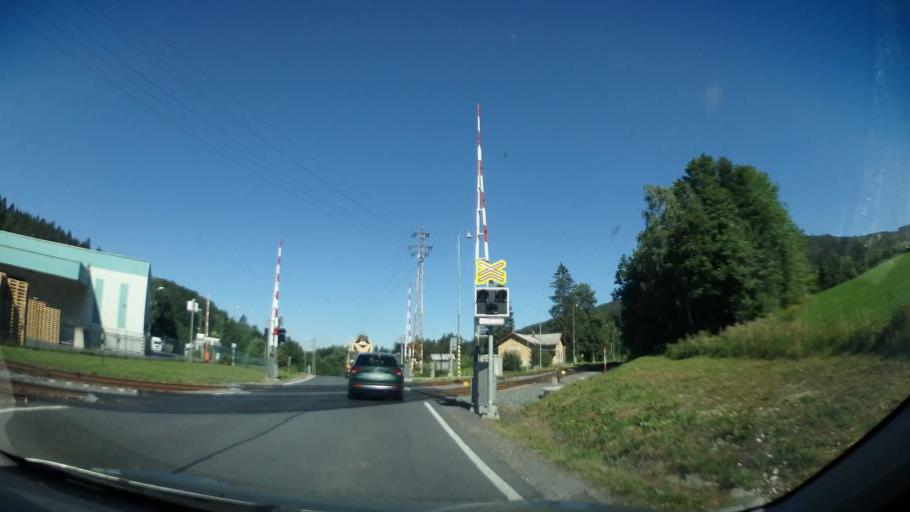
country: CZ
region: Olomoucky
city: Vapenna
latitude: 50.2437
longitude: 17.1437
